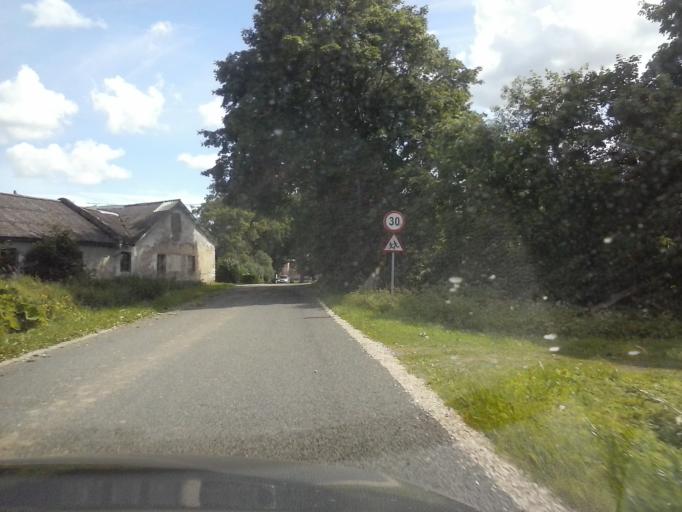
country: EE
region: Laeaene-Virumaa
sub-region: Vaeike-Maarja vald
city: Vaike-Maarja
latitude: 59.0798
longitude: 26.1953
